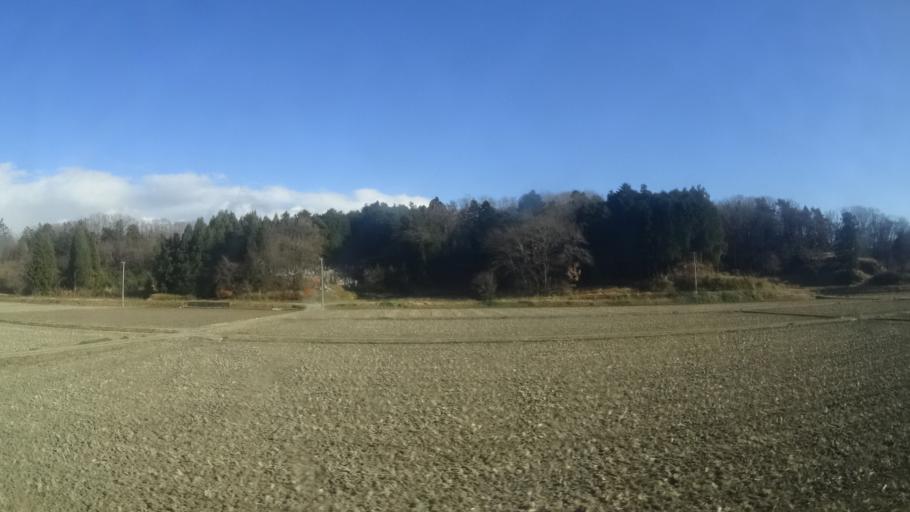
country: JP
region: Miyagi
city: Marumori
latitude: 37.8165
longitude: 140.9240
